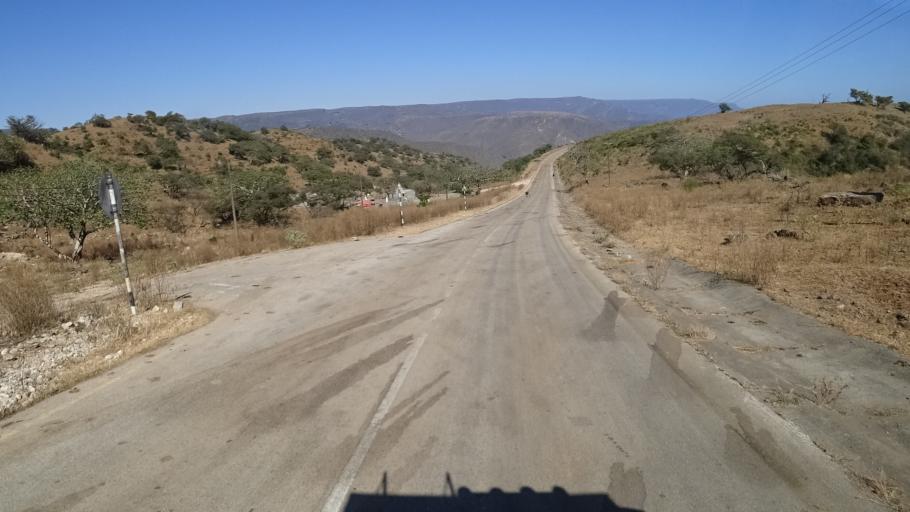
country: YE
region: Al Mahrah
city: Hawf
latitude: 16.7424
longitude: 53.3690
